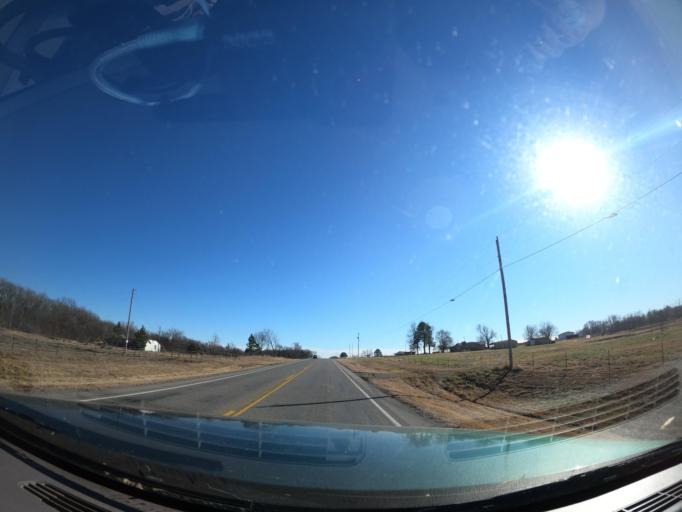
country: US
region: Oklahoma
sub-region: Muskogee County
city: Haskell
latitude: 35.7653
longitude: -95.6500
